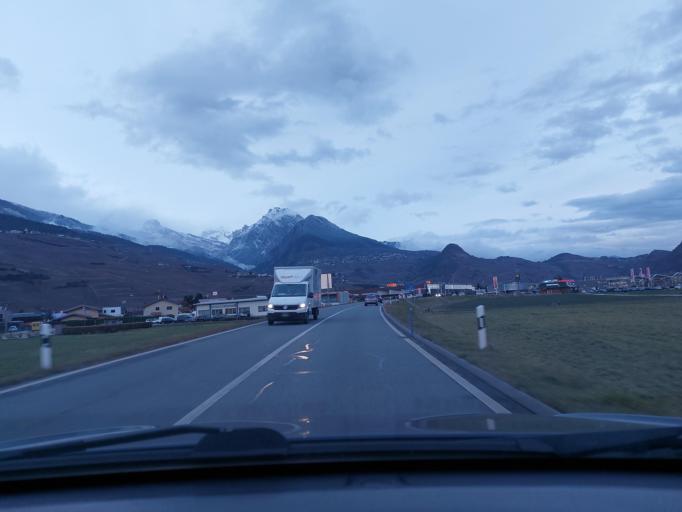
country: CH
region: Valais
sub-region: Conthey District
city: Vetroz
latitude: 46.2214
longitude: 7.2926
